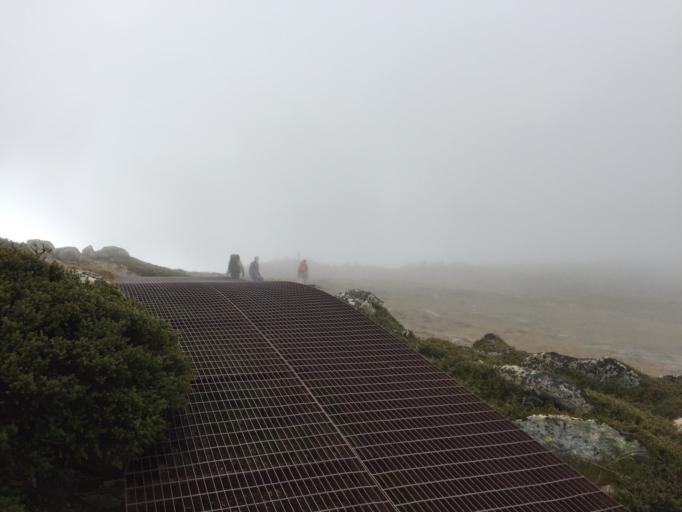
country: AU
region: New South Wales
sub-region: Snowy River
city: Jindabyne
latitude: -36.4653
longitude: 148.2698
